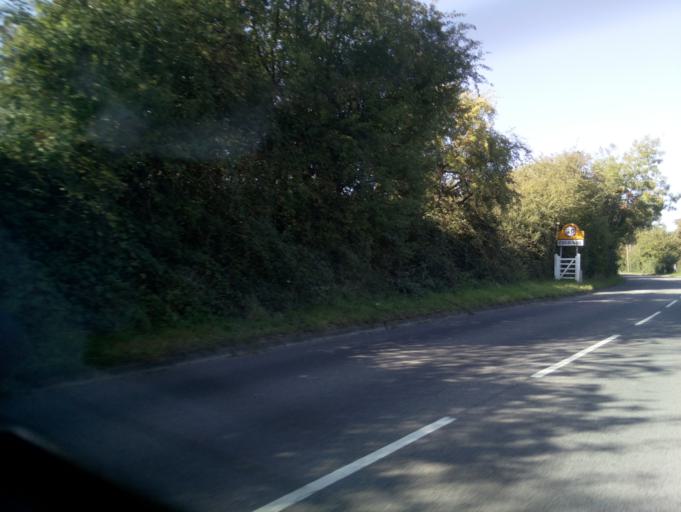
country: GB
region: England
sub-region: West Berkshire
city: Cold Ash
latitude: 51.4164
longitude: -1.2621
